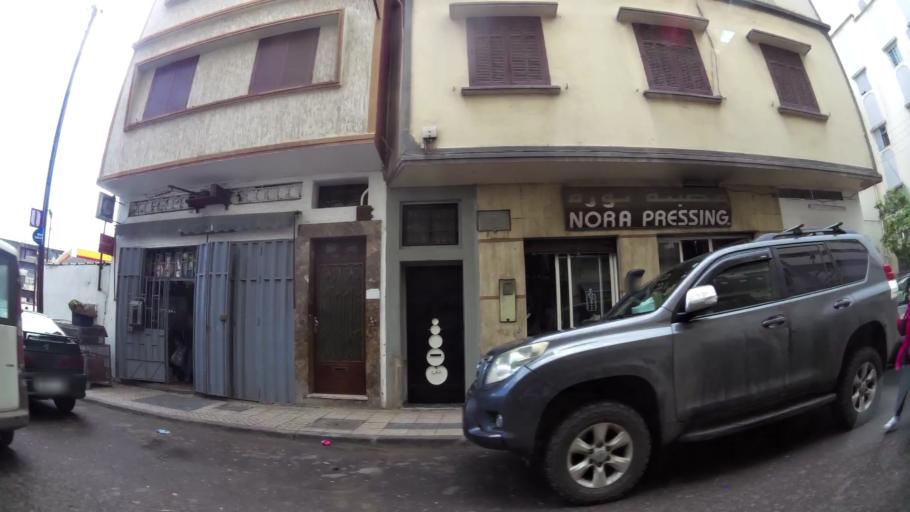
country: MA
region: Grand Casablanca
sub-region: Casablanca
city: Casablanca
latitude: 33.5662
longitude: -7.6100
